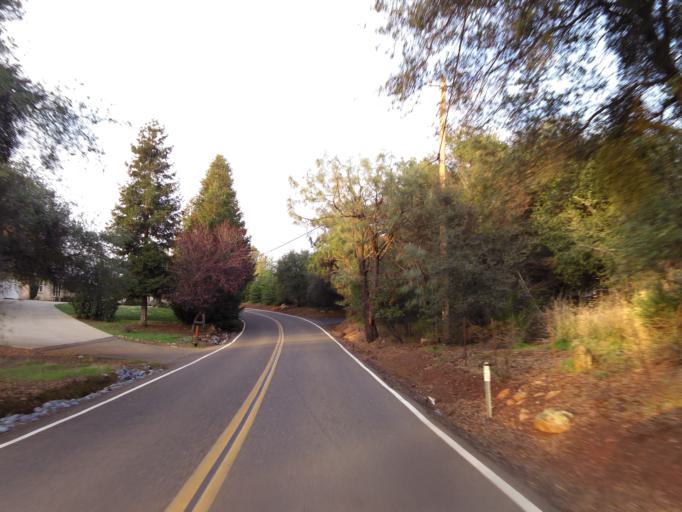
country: US
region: California
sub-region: El Dorado County
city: Cameron Park
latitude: 38.7282
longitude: -121.0049
